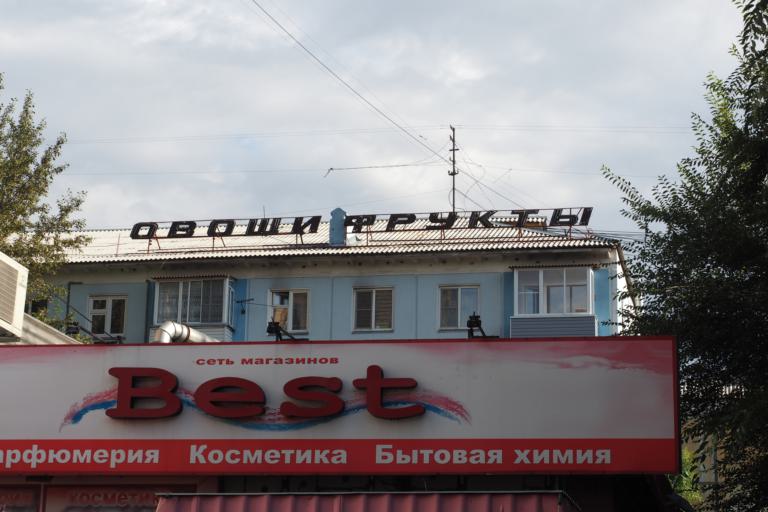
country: RU
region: Krasnoyarskiy
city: Krasnoyarsk
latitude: 55.9933
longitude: 92.8945
